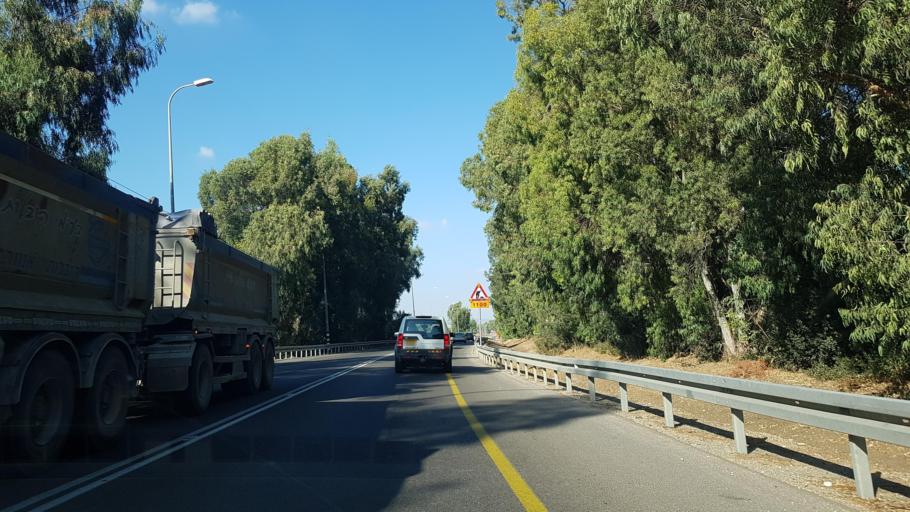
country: PS
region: West Bank
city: Tulkarm
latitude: 32.3279
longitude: 35.0021
